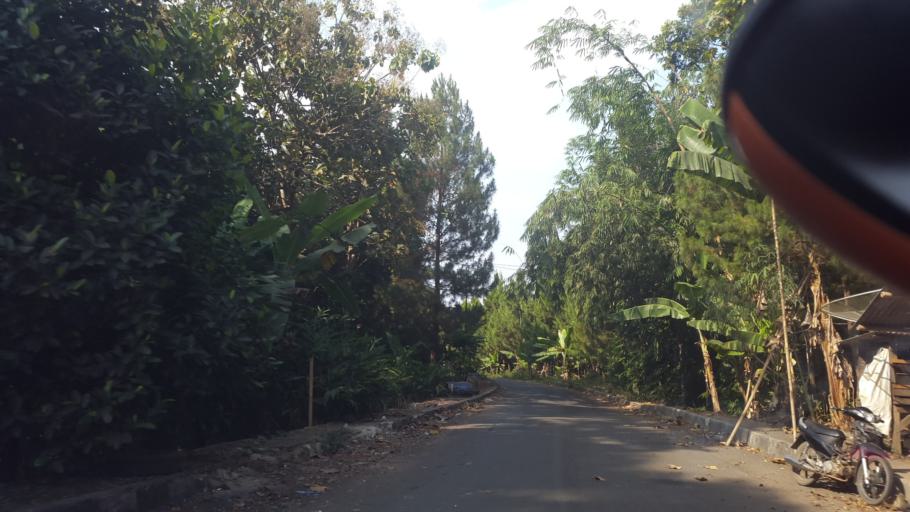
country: ID
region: West Java
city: Sumurnanjung
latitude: -7.2481
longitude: 106.9146
